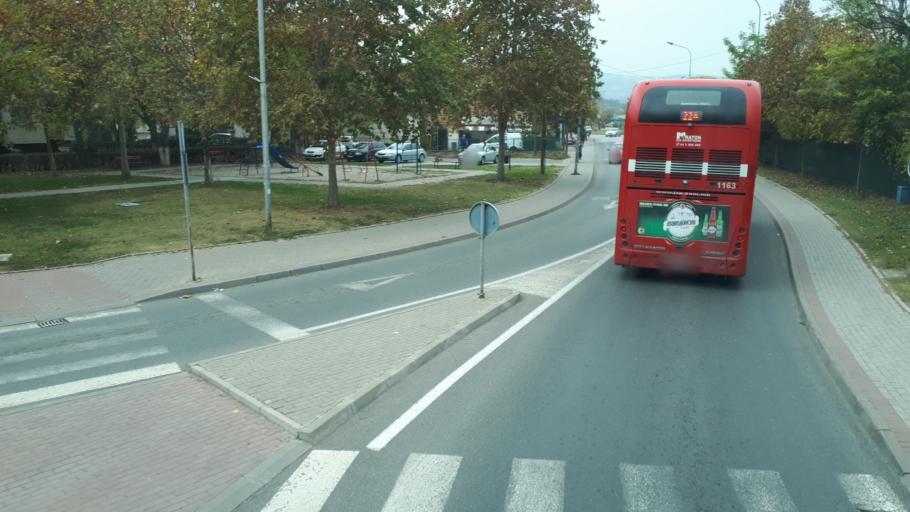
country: MK
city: Krushopek
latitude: 42.0101
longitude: 21.3613
